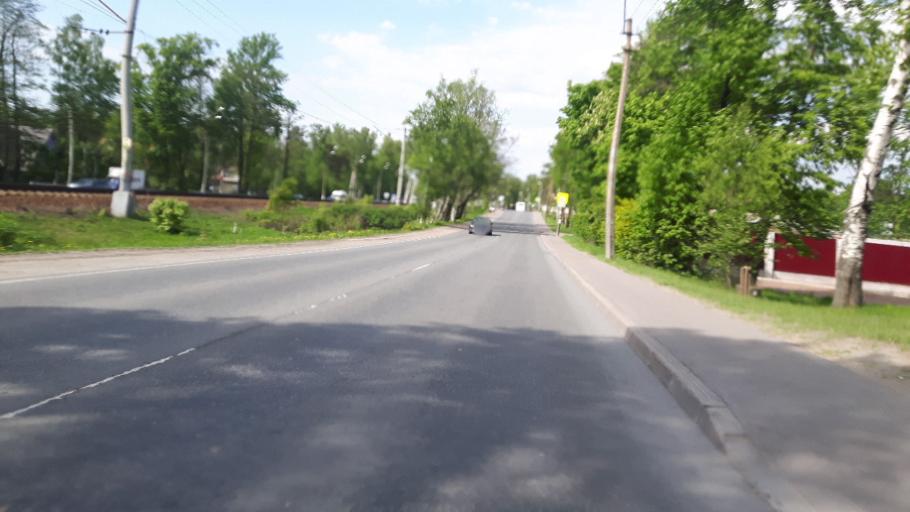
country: RU
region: St.-Petersburg
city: Aleksandrovskaya
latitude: 60.0544
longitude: 29.9778
